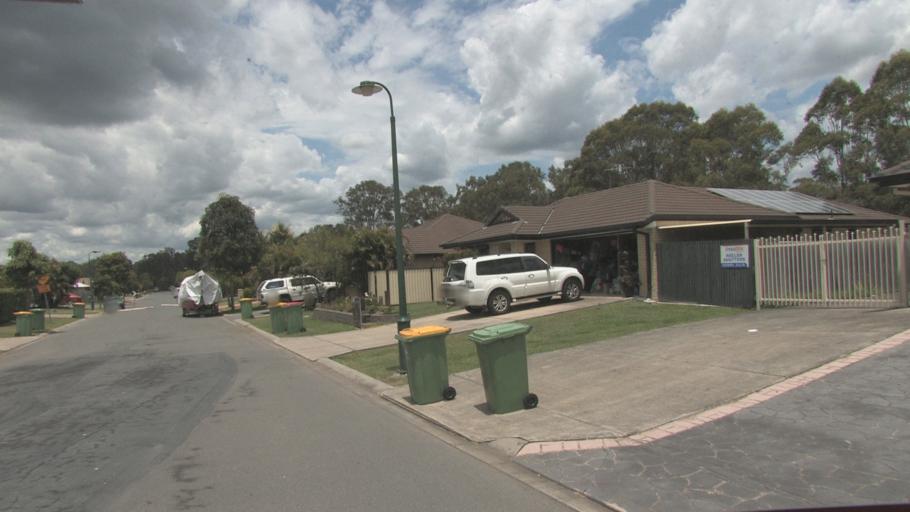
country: AU
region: Queensland
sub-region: Logan
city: Waterford West
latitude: -27.6929
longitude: 153.1117
